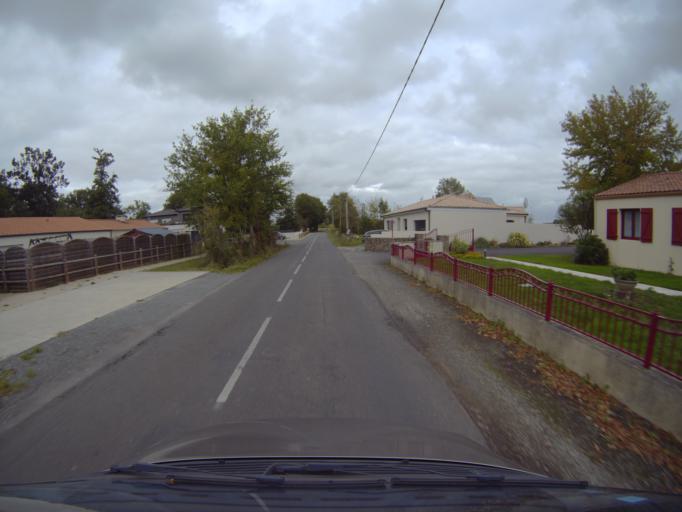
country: FR
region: Pays de la Loire
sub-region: Departement de la Loire-Atlantique
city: Clisson
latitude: 47.1034
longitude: -1.2662
